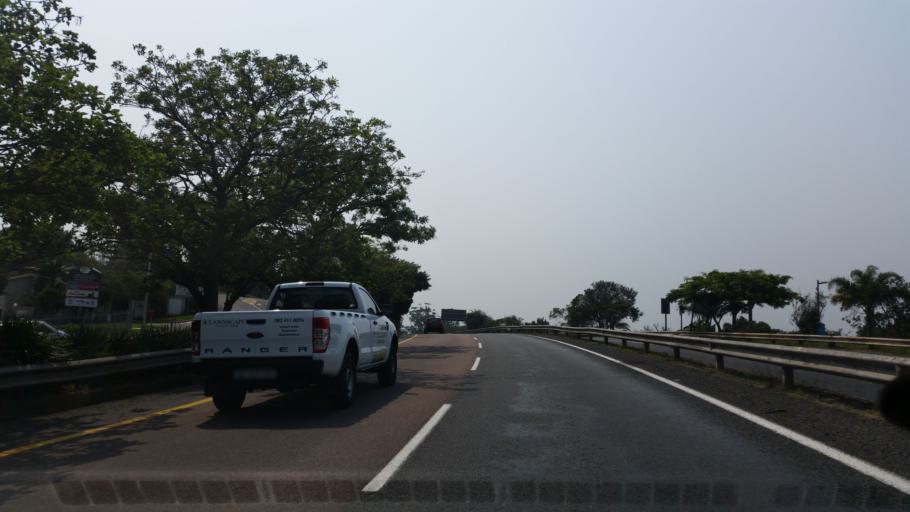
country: ZA
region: KwaZulu-Natal
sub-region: eThekwini Metropolitan Municipality
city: Berea
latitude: -29.8345
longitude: 30.9193
